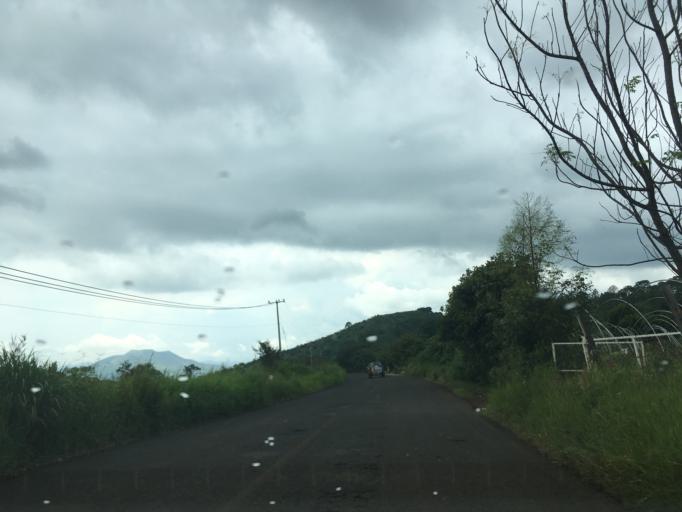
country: MX
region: Michoacan
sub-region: Periban
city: Gildardo Magana (Los Angeles)
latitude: 19.5827
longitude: -102.4329
